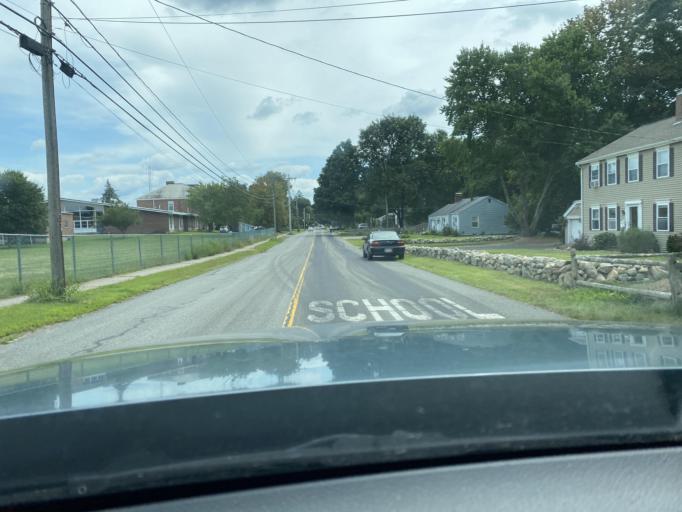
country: US
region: Massachusetts
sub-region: Norfolk County
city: Medfield
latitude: 42.1931
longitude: -71.3129
